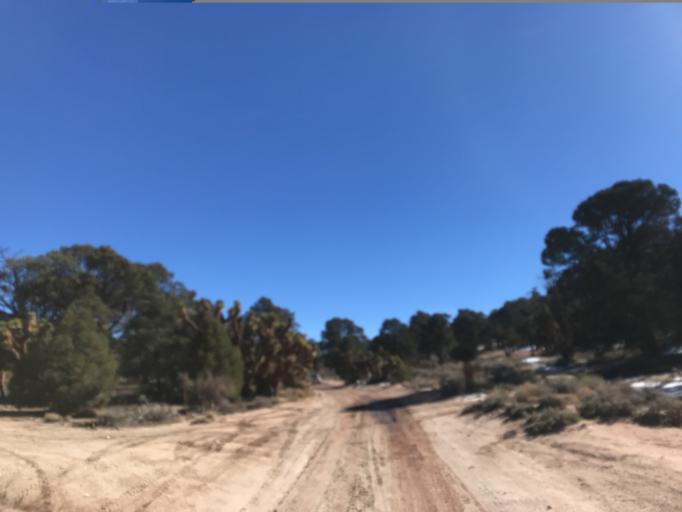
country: US
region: California
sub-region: San Bernardino County
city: Big Bear City
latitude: 34.2430
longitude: -116.6990
